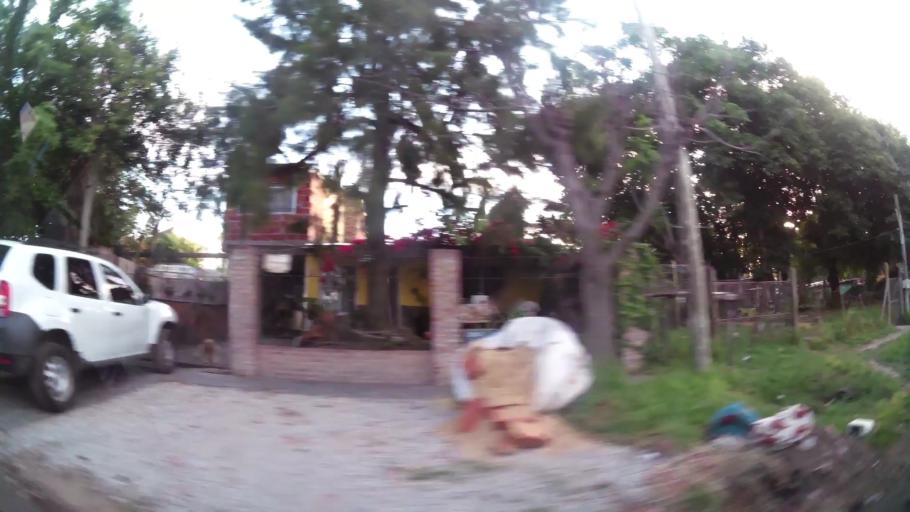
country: AR
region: Buenos Aires
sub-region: Partido de Tigre
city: Tigre
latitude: -34.4502
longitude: -58.6555
